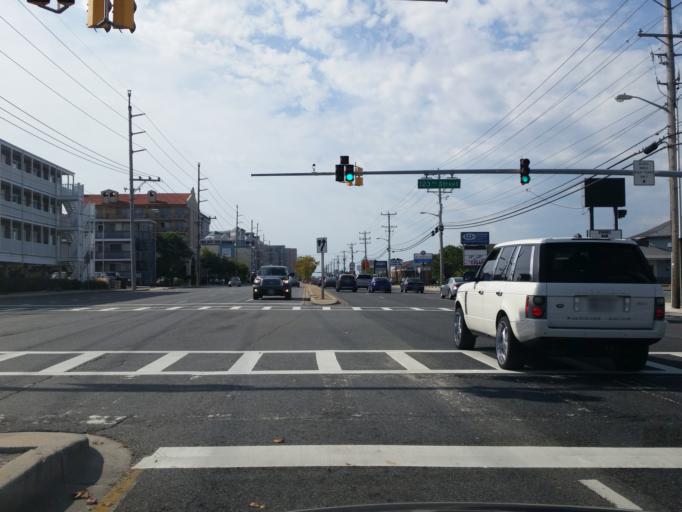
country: US
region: Maryland
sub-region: Worcester County
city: Ocean City
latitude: 38.4285
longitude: -75.0554
